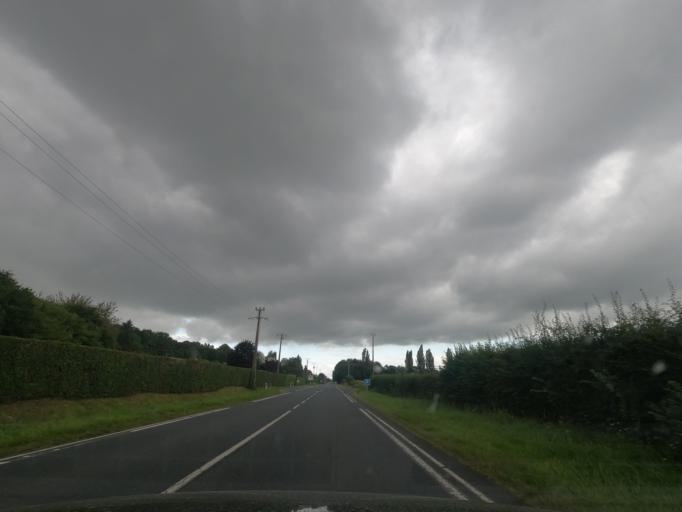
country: FR
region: Lower Normandy
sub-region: Departement de l'Orne
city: Argentan
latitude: 48.7568
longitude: 0.0707
